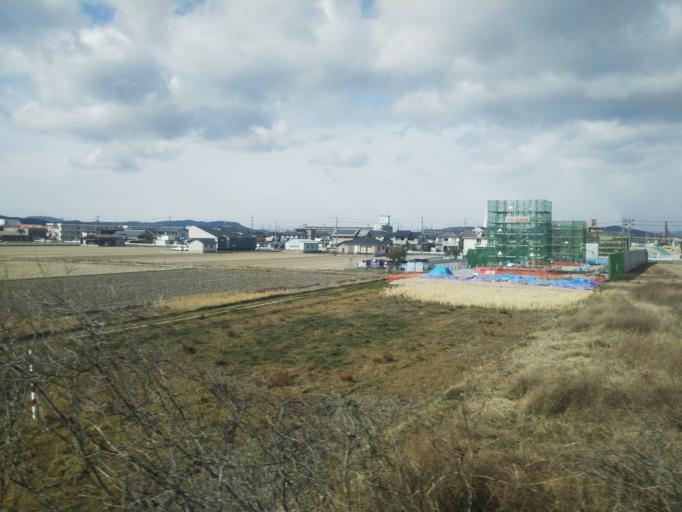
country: JP
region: Okayama
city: Okayama-shi
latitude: 34.6124
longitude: 133.8800
